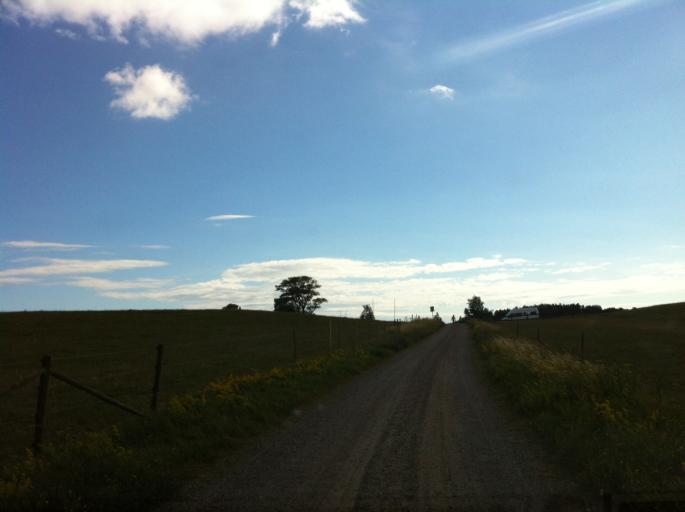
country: SE
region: Skane
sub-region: Ystads Kommun
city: Kopingebro
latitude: 55.3905
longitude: 14.0521
